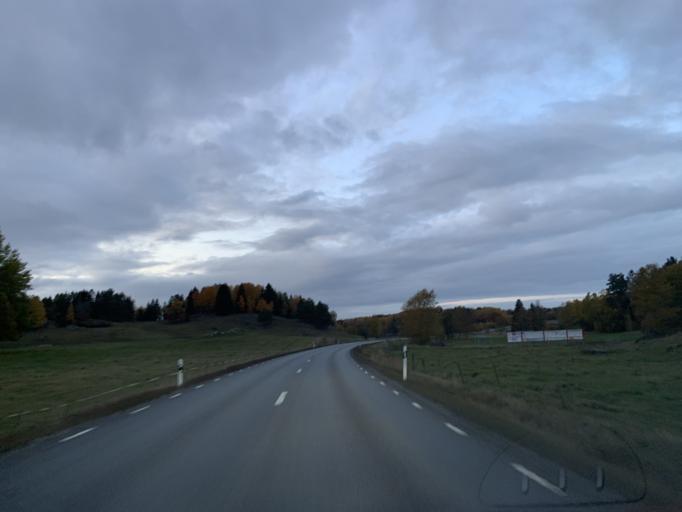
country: SE
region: Stockholm
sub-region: Nynashamns Kommun
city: Osmo
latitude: 59.0212
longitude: 17.7985
